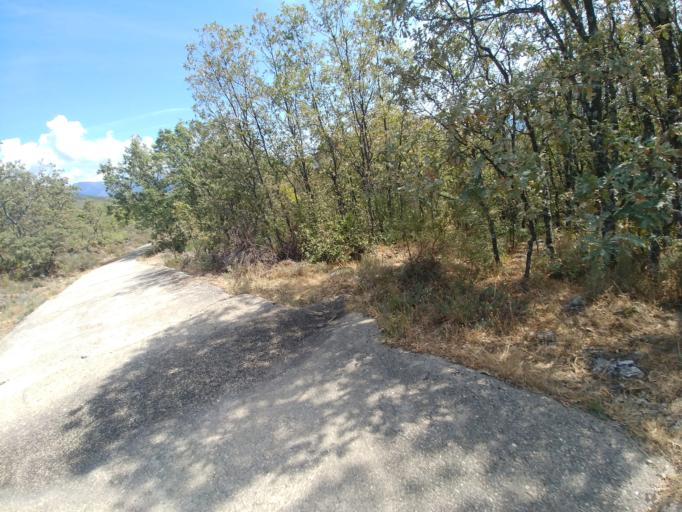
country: ES
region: Extremadura
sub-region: Provincia de Caceres
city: Garganta la Olla
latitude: 40.1100
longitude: -5.7484
